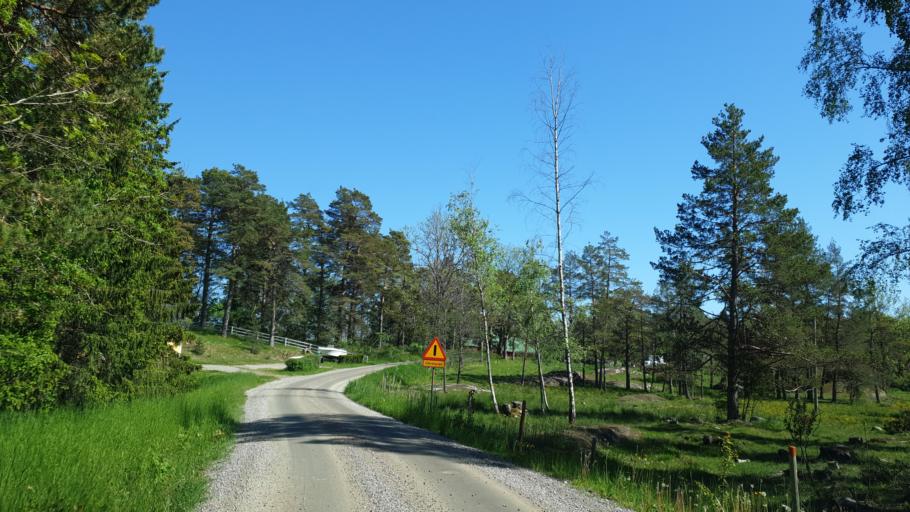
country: SE
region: Soedermanland
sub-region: Trosa Kommun
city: Vagnharad
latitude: 58.9229
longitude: 17.5153
